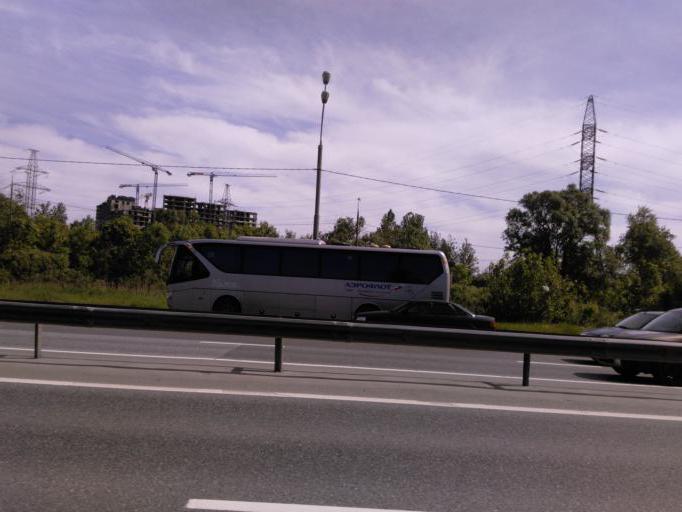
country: RU
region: Moscow
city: Khimki
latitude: 55.9128
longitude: 37.4035
